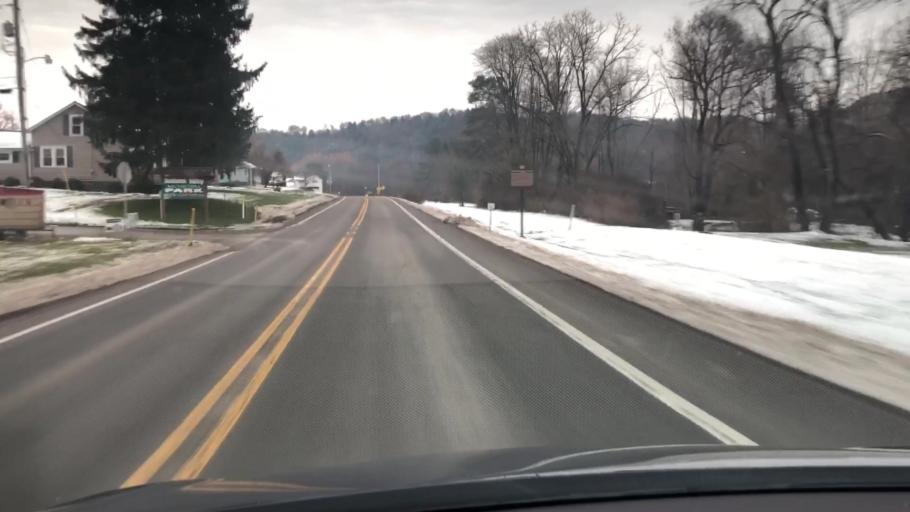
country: US
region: Pennsylvania
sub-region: Clarion County
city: Clarion
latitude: 41.0127
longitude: -79.2942
